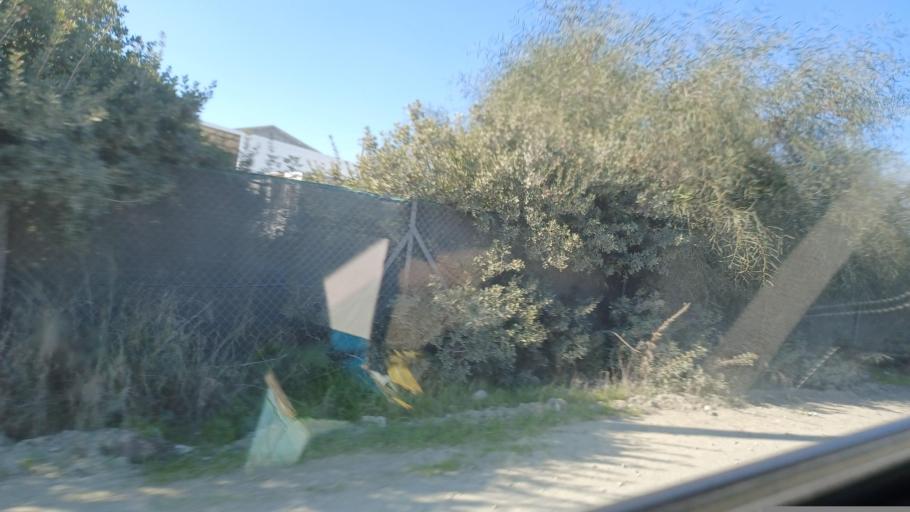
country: CY
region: Lefkosia
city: Alampra
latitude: 35.0199
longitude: 33.3809
